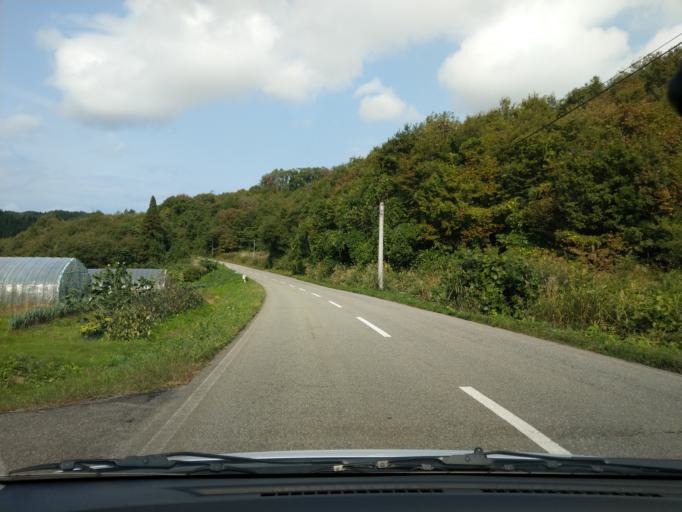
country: JP
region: Akita
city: Omagari
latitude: 39.4921
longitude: 140.3136
